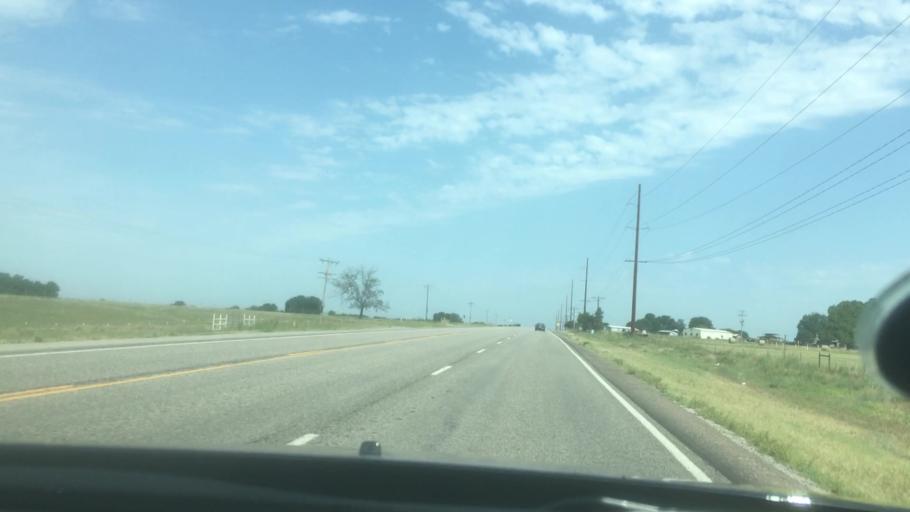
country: US
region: Oklahoma
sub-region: Seminole County
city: Konawa
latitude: 34.8484
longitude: -96.8076
